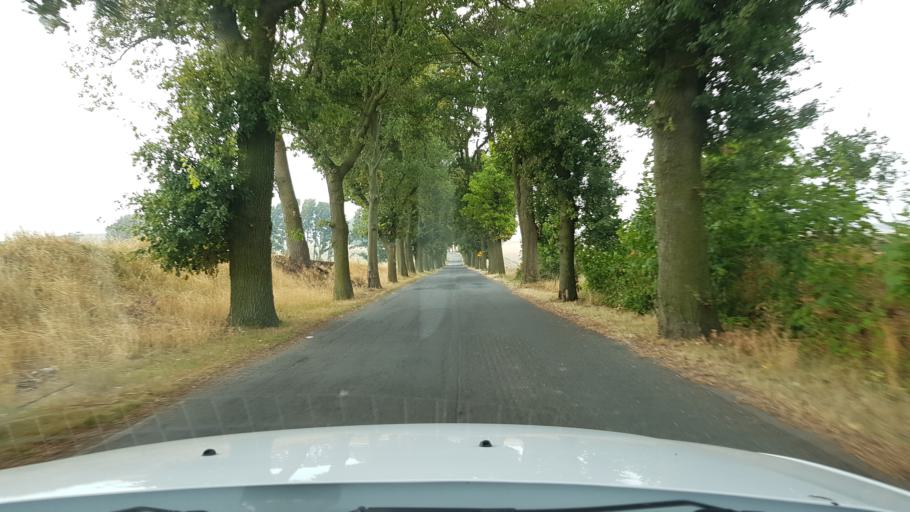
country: PL
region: West Pomeranian Voivodeship
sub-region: Powiat gryfinski
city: Moryn
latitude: 52.8895
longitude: 14.3781
